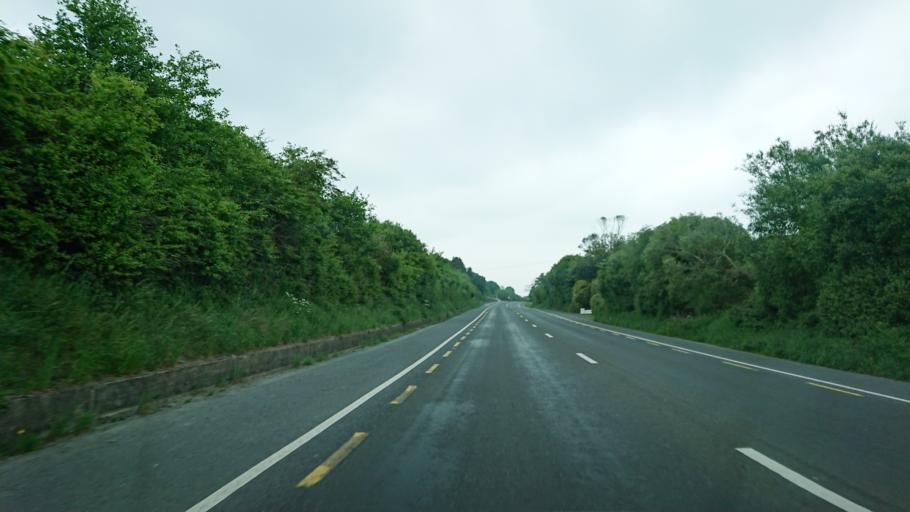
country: IE
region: Munster
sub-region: Waterford
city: Tra Mhor
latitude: 52.1899
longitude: -7.1272
